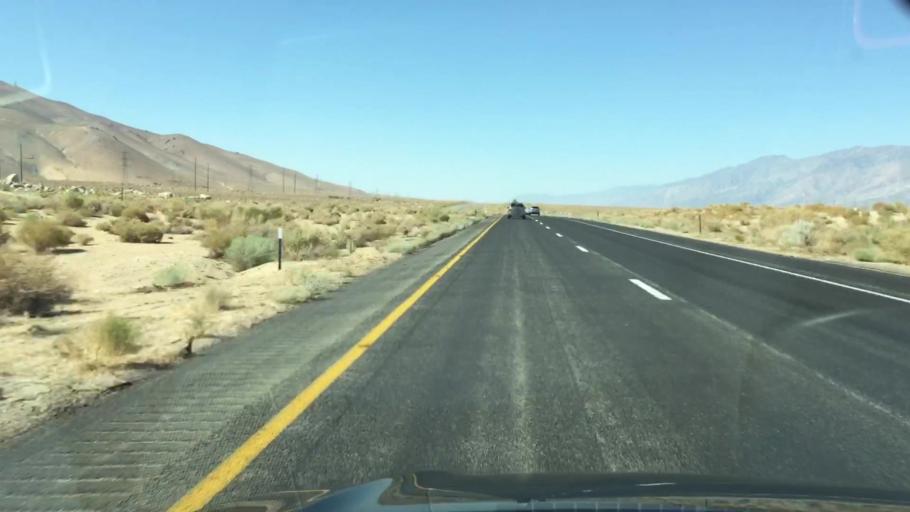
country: US
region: California
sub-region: Inyo County
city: Lone Pine
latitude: 36.4230
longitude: -118.0298
